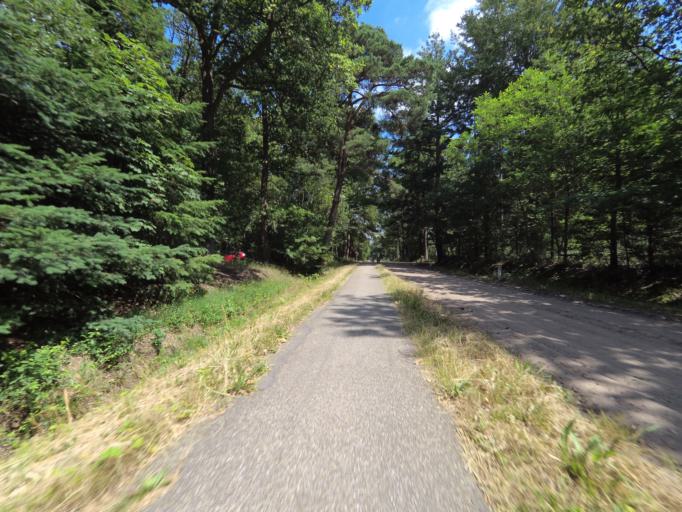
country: NL
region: Overijssel
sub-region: Gemeente Wierden
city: Wierden
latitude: 52.3480
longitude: 6.5199
